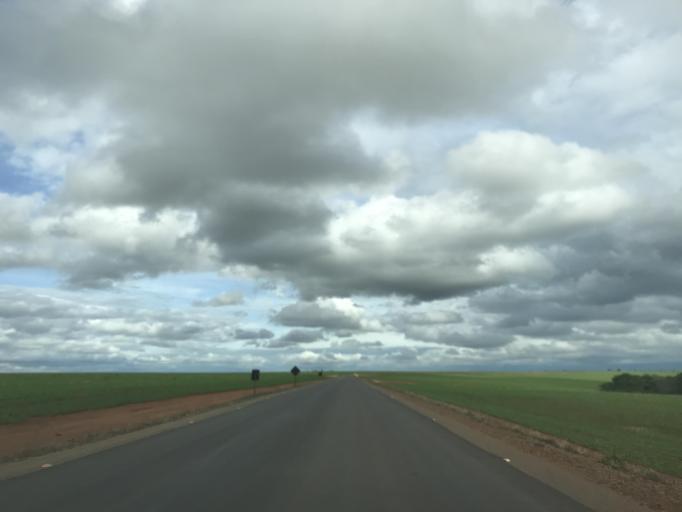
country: BR
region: Goias
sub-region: Vianopolis
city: Vianopolis
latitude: -16.9594
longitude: -48.6353
